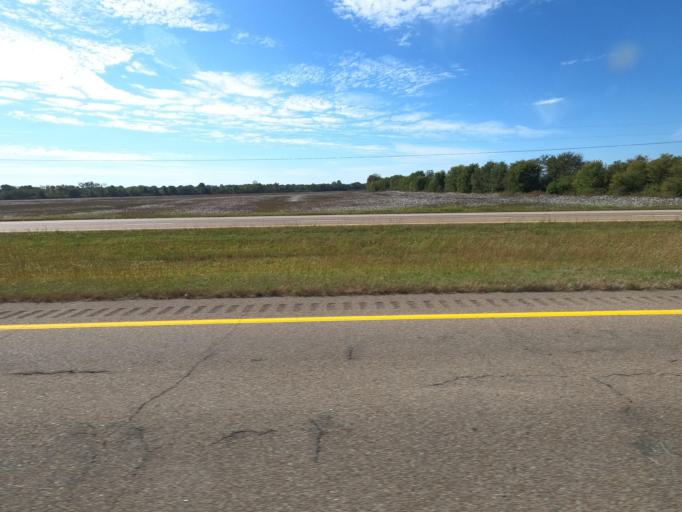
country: US
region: Tennessee
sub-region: Crockett County
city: Alamo
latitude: 35.8544
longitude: -89.1991
